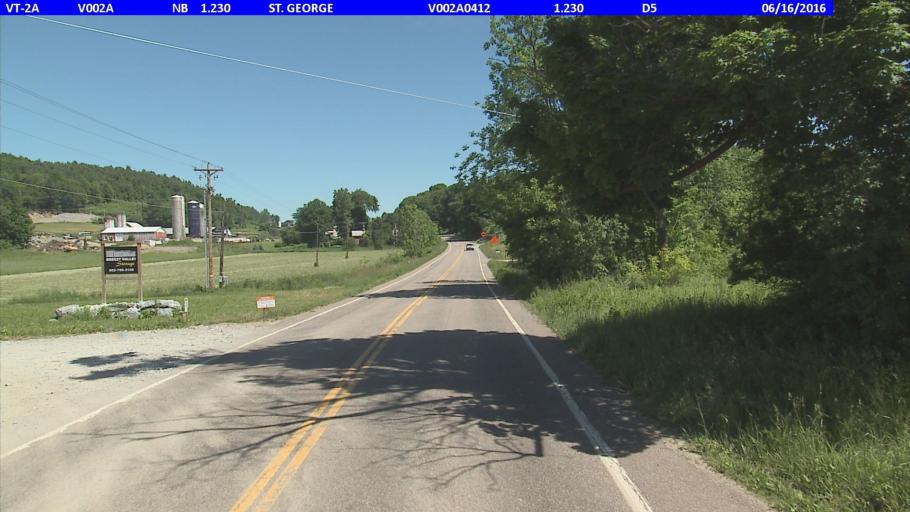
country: US
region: Vermont
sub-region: Chittenden County
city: Hinesburg
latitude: 44.3872
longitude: -73.1277
